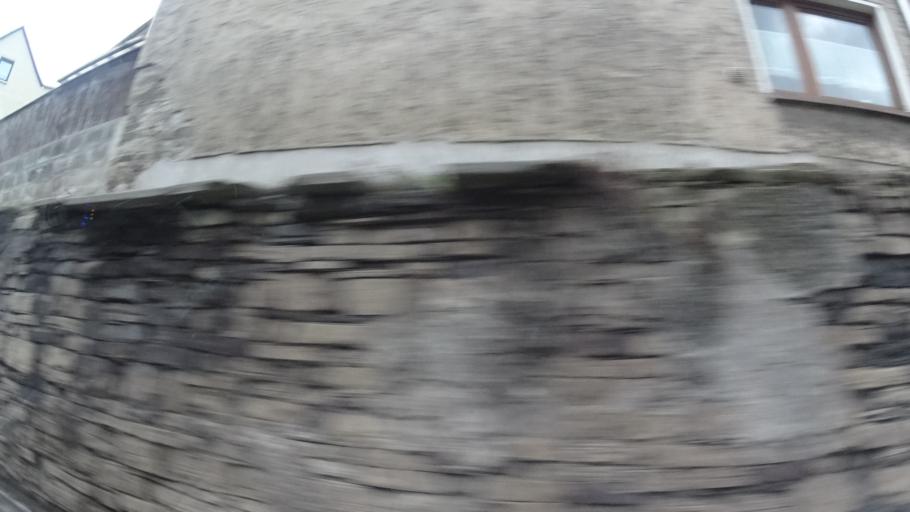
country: DE
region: Thuringia
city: Auma
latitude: 50.7005
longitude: 11.9007
